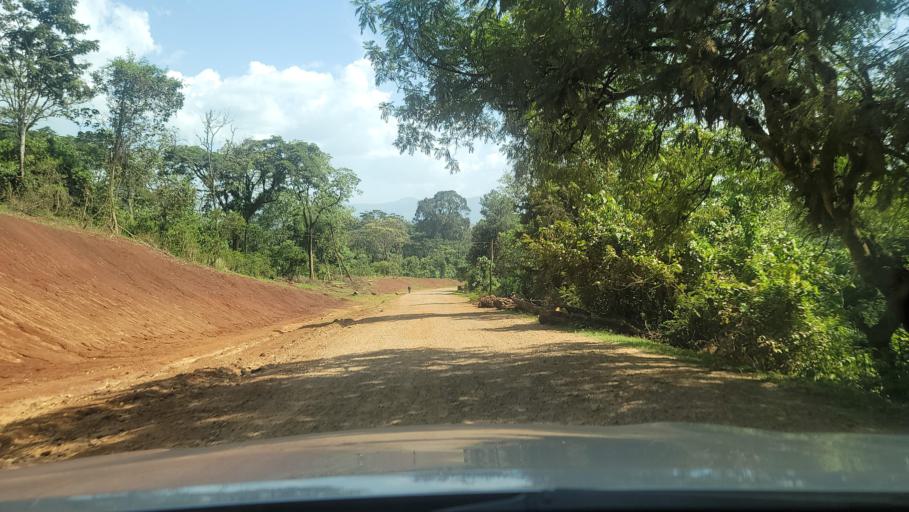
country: ET
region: Oromiya
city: Agaro
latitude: 7.7928
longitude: 36.4357
